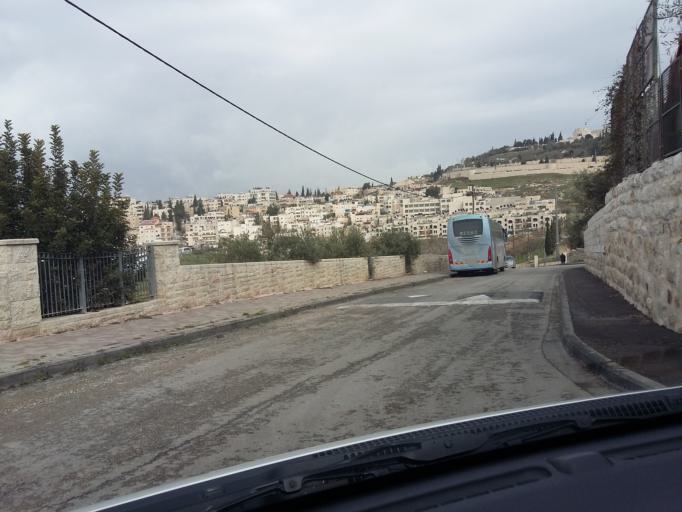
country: PS
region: West Bank
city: East Jerusalem
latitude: 31.7851
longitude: 35.2404
